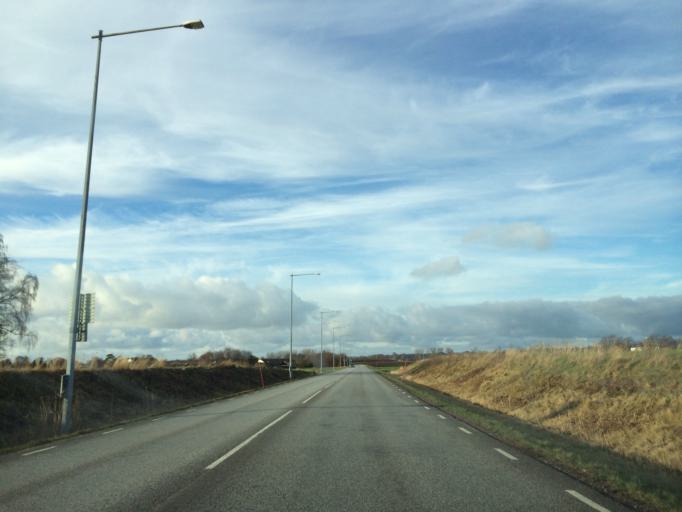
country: SE
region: Skane
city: Bjarred
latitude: 55.7229
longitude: 13.0419
